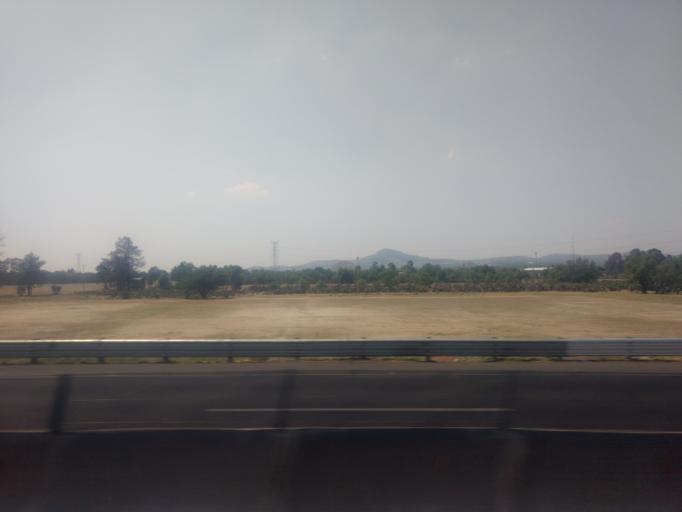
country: MX
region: Morelos
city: San Martin de las Piramides
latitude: 19.6822
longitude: -98.8201
